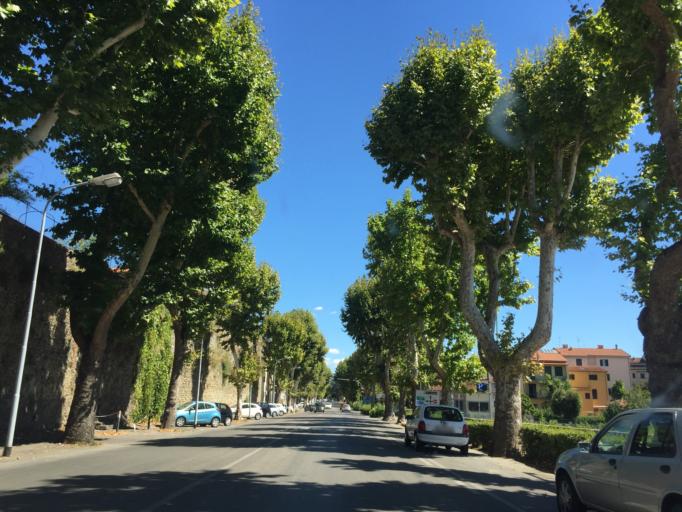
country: IT
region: Tuscany
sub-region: Provincia di Pistoia
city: Pistoia
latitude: 43.9382
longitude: 10.9186
